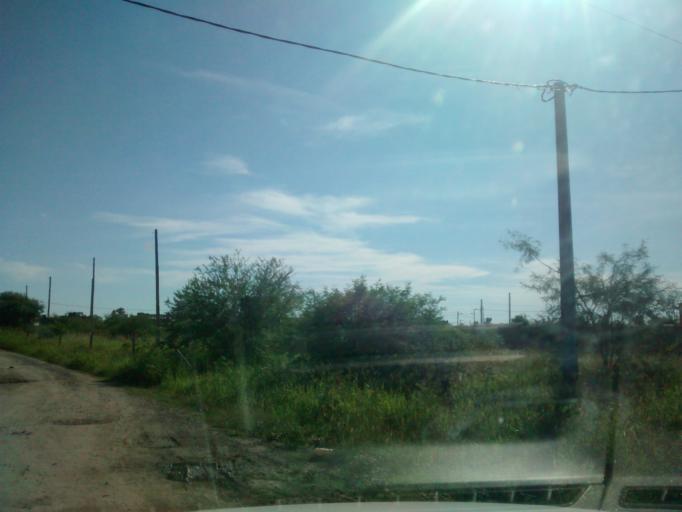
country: AR
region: Chaco
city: Fontana
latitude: -27.4049
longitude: -58.9883
